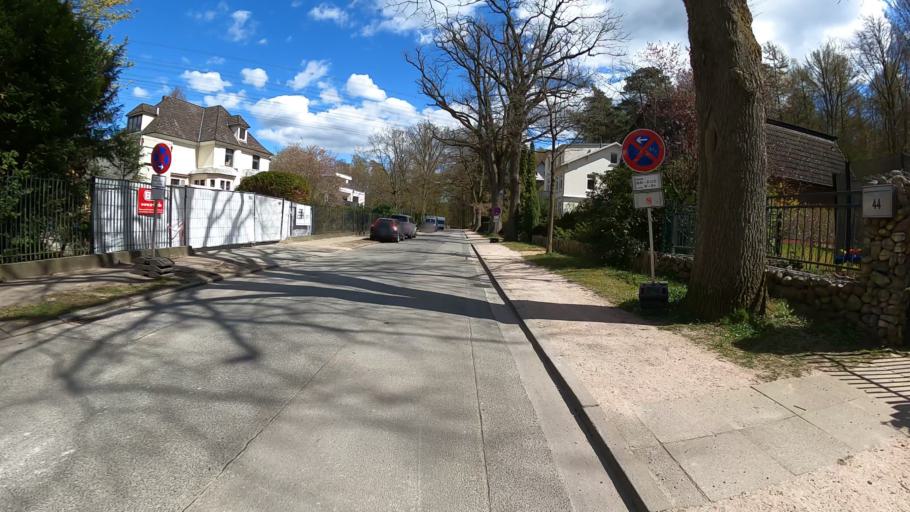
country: DE
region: Hamburg
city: Bergedorf
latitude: 53.4960
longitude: 10.2320
